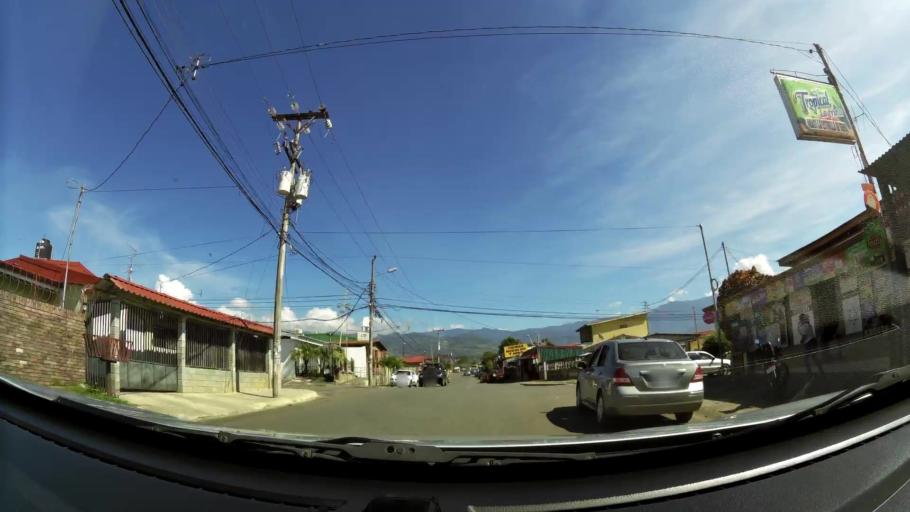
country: CR
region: San Jose
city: San Isidro
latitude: 9.3690
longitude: -83.7123
